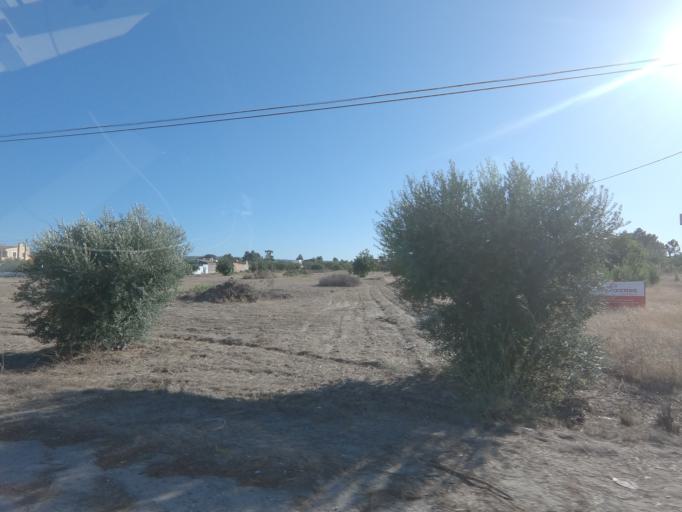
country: PT
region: Setubal
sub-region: Palmela
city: Quinta do Anjo
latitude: 38.5995
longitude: -8.9346
